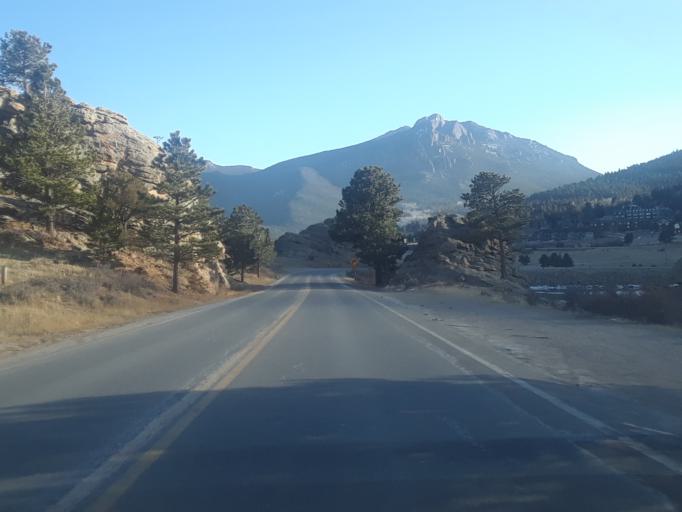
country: US
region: Colorado
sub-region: Larimer County
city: Estes Park
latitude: 40.3444
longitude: -105.5299
